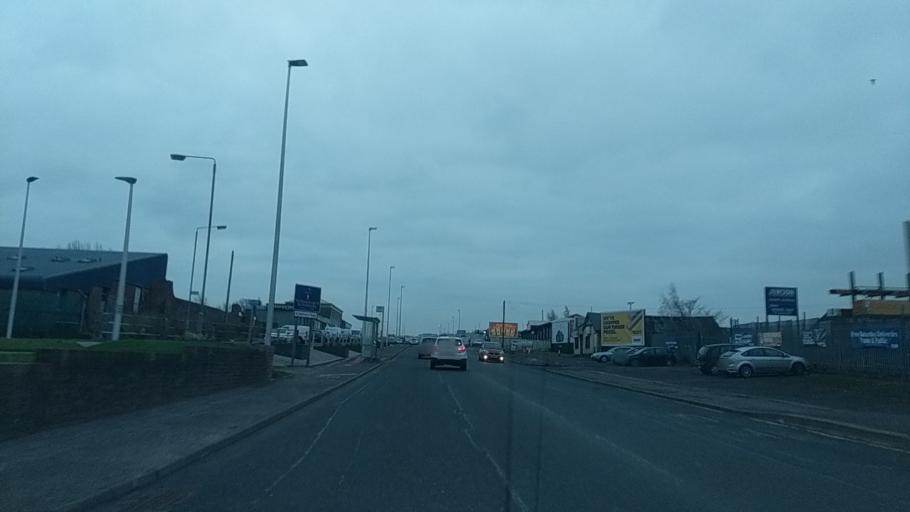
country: GB
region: Scotland
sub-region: South Lanarkshire
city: Rutherglen
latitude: 55.8361
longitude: -4.2269
